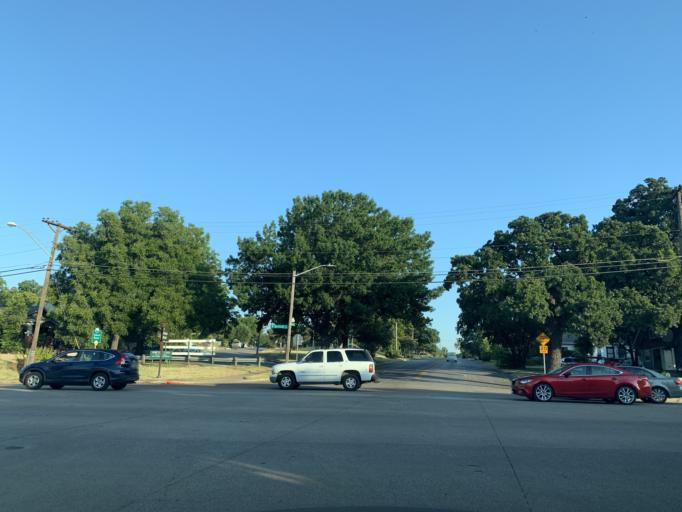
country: US
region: Texas
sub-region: Tarrant County
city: River Oaks
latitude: 32.7695
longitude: -97.3555
